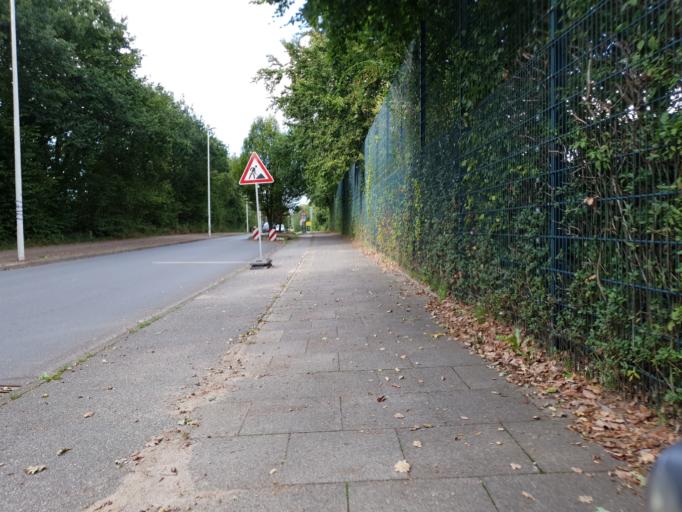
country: DE
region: Schleswig-Holstein
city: Kronshagen
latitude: 54.3417
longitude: 10.0811
